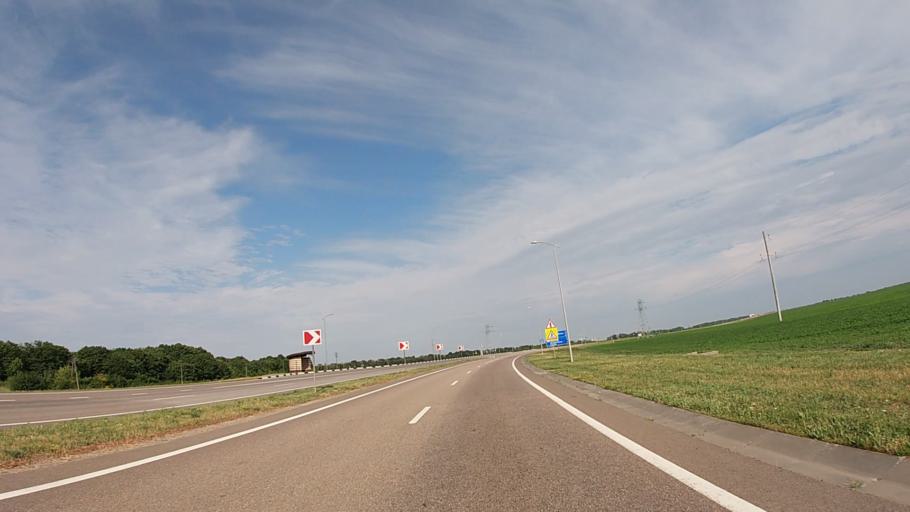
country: RU
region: Belgorod
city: Rakitnoye
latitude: 50.7904
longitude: 35.8704
